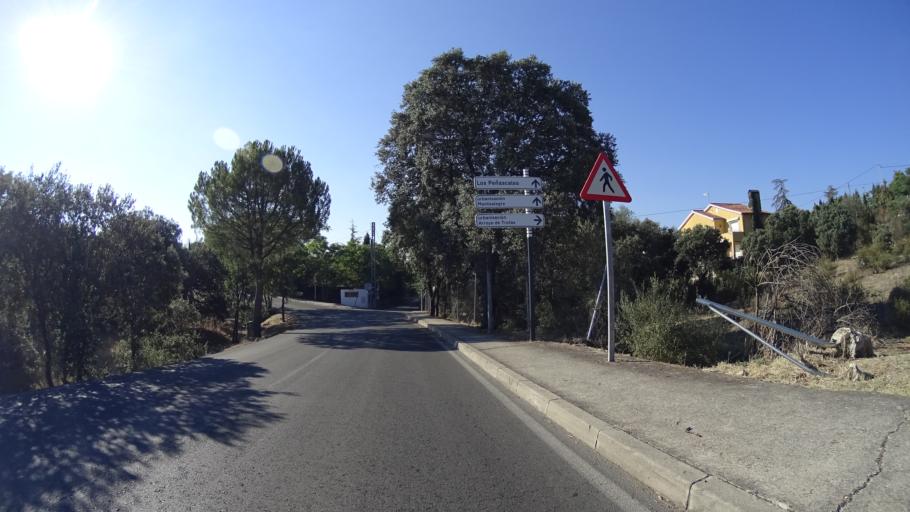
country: ES
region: Madrid
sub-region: Provincia de Madrid
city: Torrelodones
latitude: 40.5822
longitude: -3.9105
